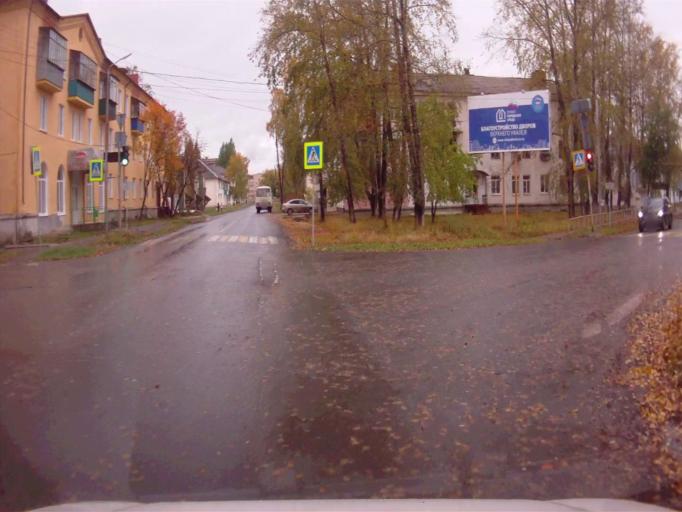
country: RU
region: Chelyabinsk
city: Verkhniy Ufaley
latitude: 56.0342
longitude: 60.2621
